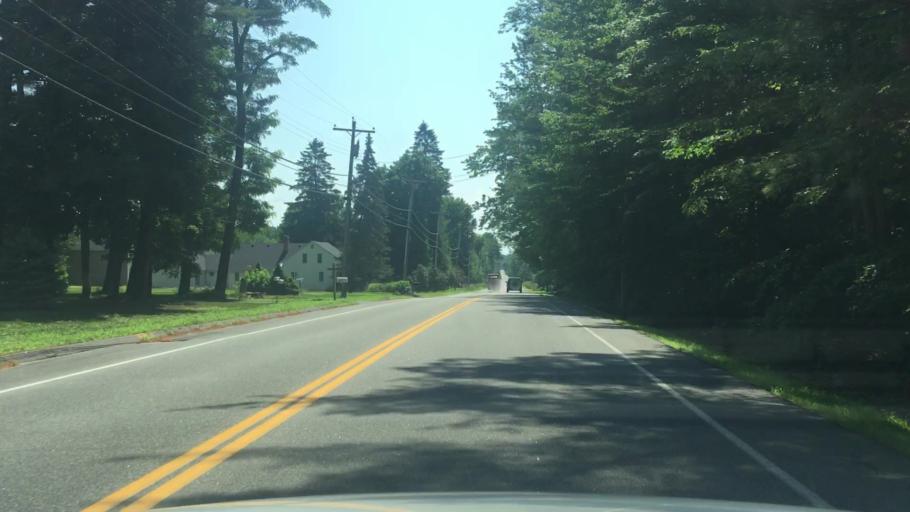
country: US
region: Maine
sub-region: Cumberland County
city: Cumberland Center
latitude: 43.8096
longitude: -70.2848
